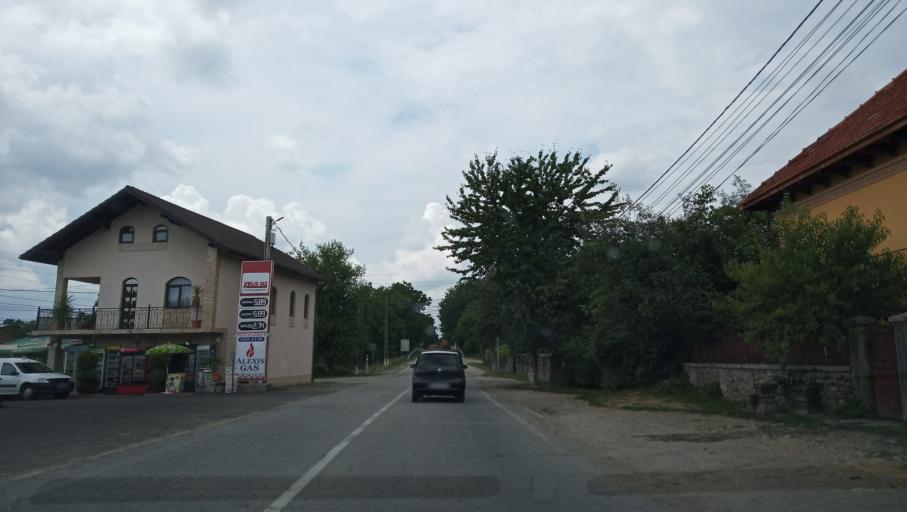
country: RO
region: Gorj
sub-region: Comuna Pestisani
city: Pestisani
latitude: 45.0800
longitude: 23.0516
